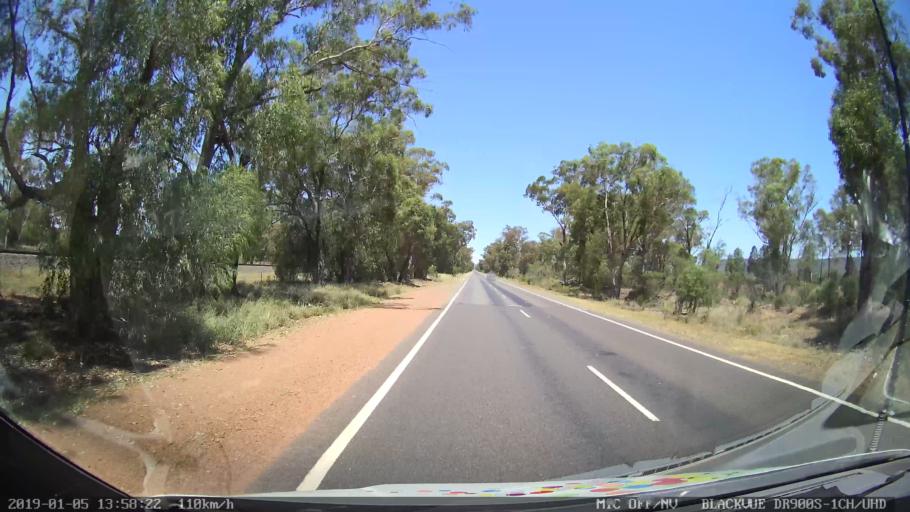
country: AU
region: New South Wales
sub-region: Gunnedah
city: Gunnedah
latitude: -31.1382
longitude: 150.2847
